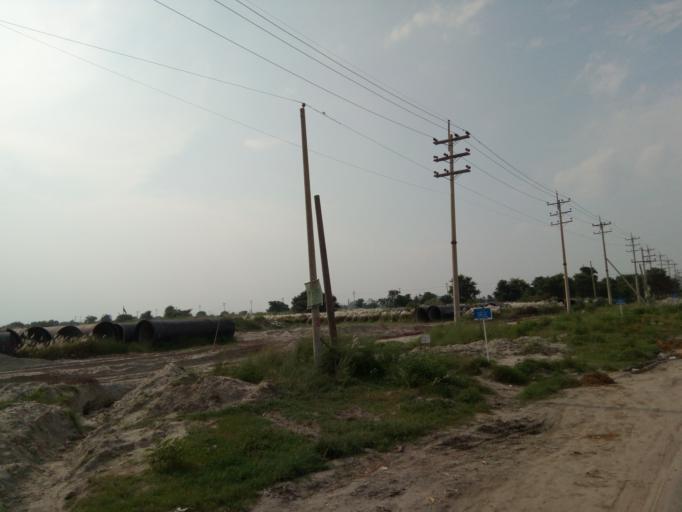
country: BD
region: Dhaka
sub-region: Dhaka
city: Dhaka
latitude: 23.6782
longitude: 90.4039
